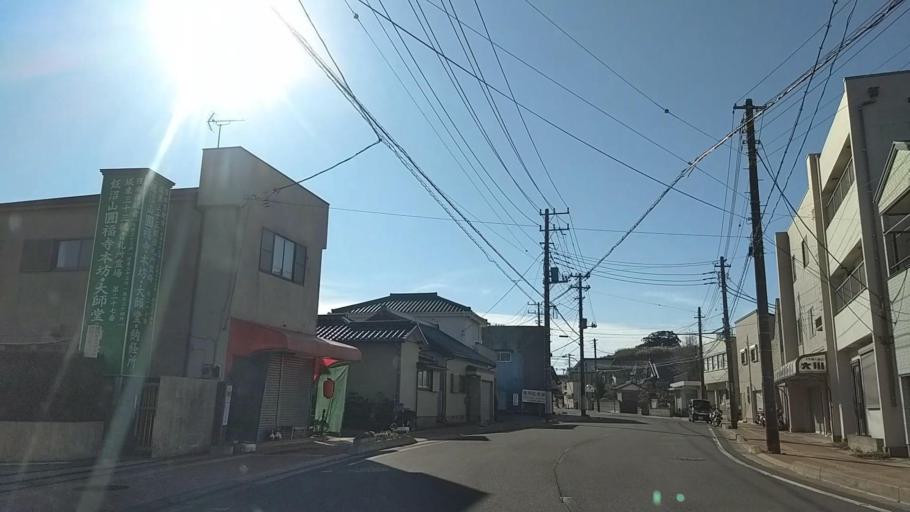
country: JP
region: Chiba
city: Hasaki
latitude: 35.7302
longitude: 140.8407
